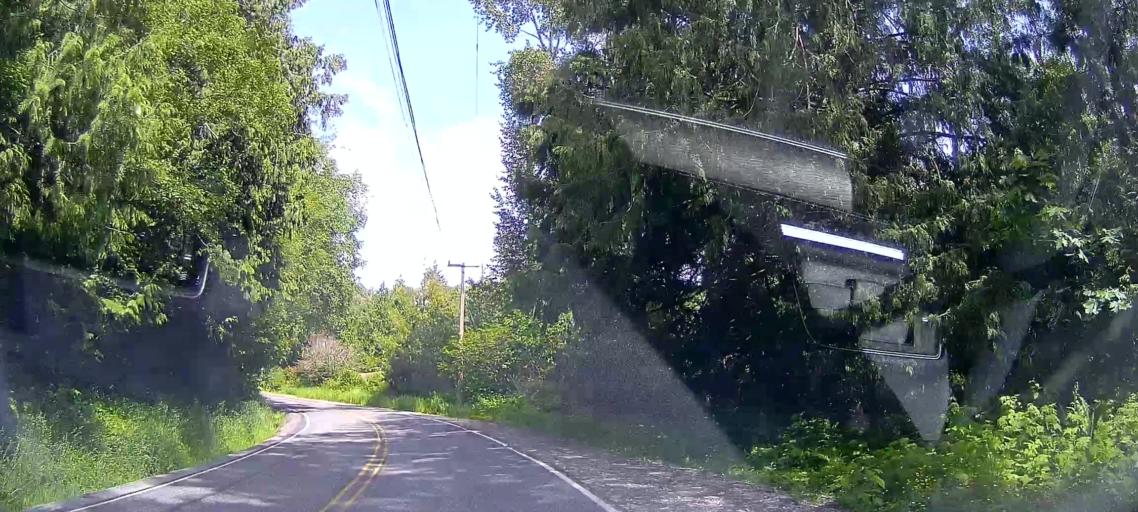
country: US
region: Washington
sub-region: Skagit County
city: Burlington
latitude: 48.5703
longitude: -122.3900
